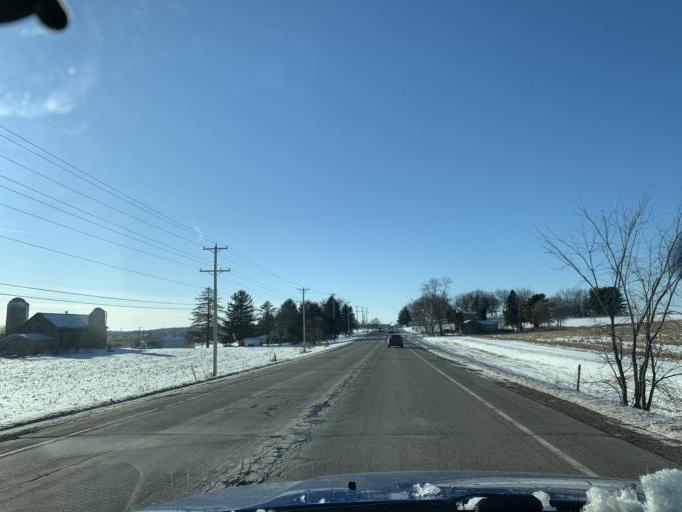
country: US
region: Wisconsin
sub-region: Dane County
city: Middleton
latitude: 43.0603
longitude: -89.5470
